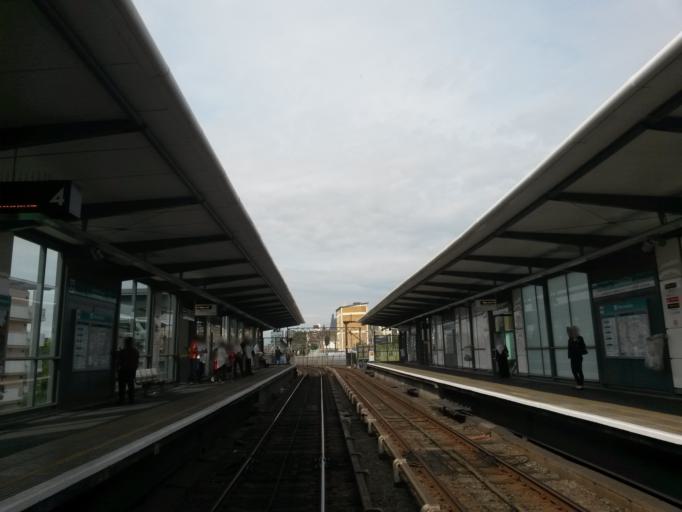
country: GB
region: England
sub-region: Greater London
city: Poplar
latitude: 51.5124
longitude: -0.0392
